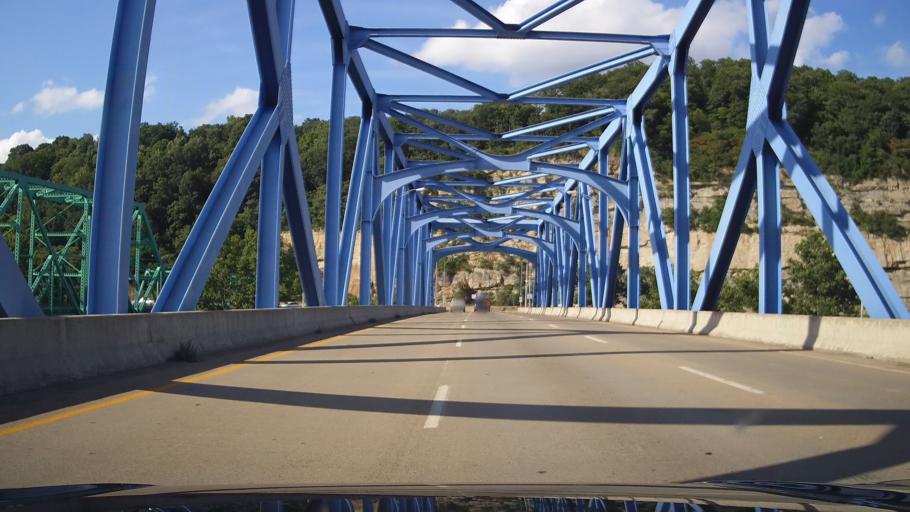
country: US
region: Kentucky
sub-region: Boyd County
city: Ashland
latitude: 38.4849
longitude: -82.6396
